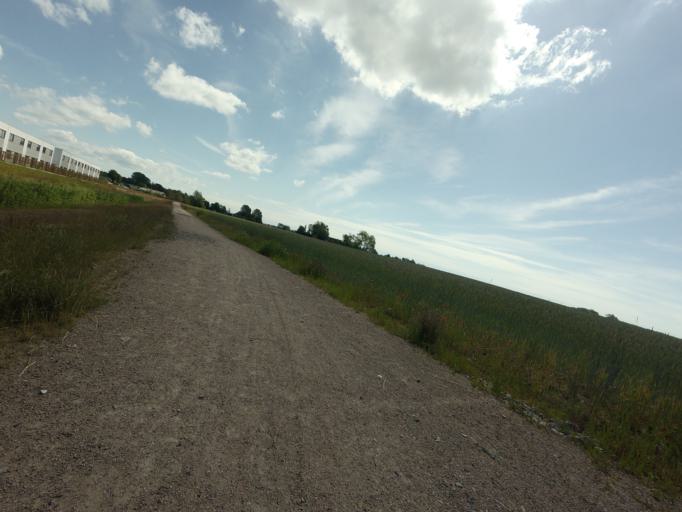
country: SE
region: Skane
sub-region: Trelleborgs Kommun
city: Skare
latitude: 55.4035
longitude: 13.0862
